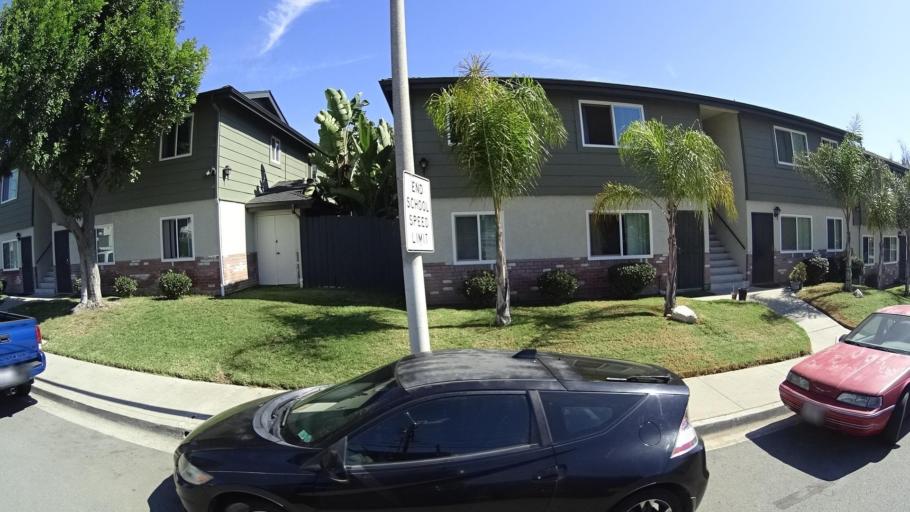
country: US
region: California
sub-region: San Diego County
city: La Presa
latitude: 32.7138
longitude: -117.0060
